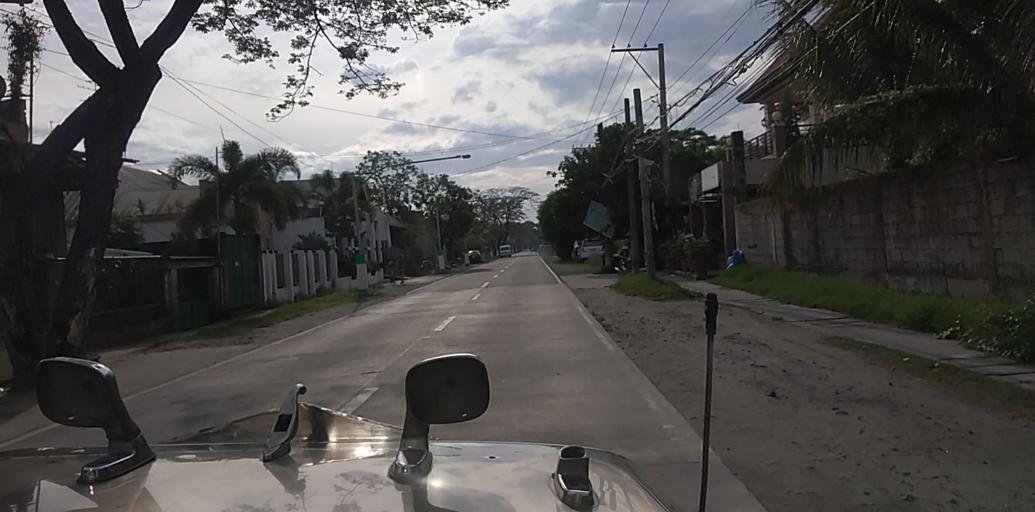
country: PH
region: Central Luzon
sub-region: Province of Pampanga
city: Minalin
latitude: 14.9784
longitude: 120.6897
